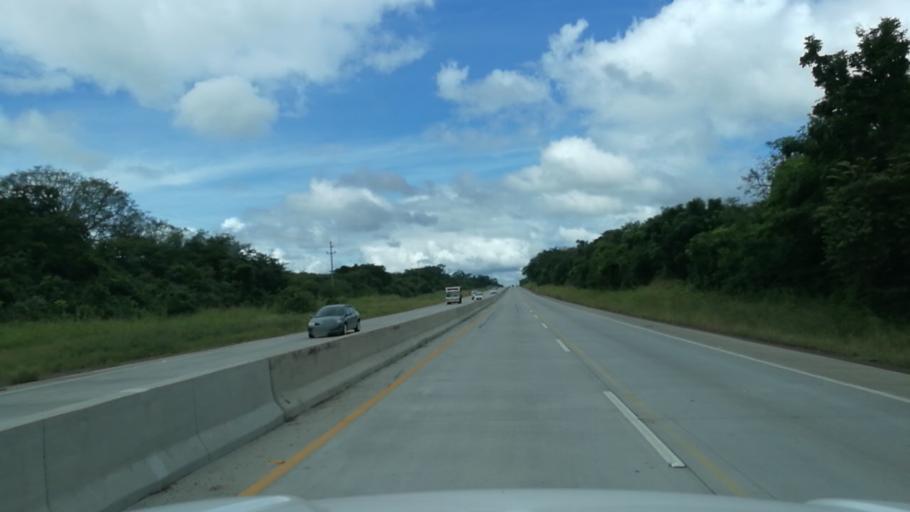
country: CR
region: Guanacaste
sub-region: Canton de Canas
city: Canas
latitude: 10.4634
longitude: -85.1511
